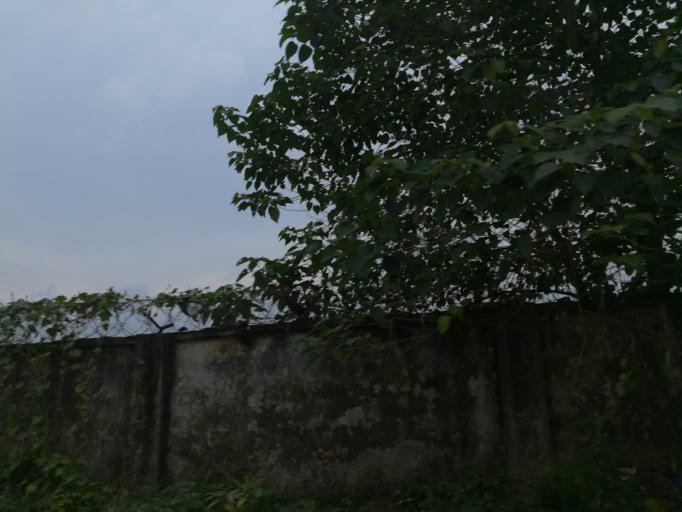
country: NG
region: Rivers
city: Okrika
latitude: 4.7834
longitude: 7.1285
